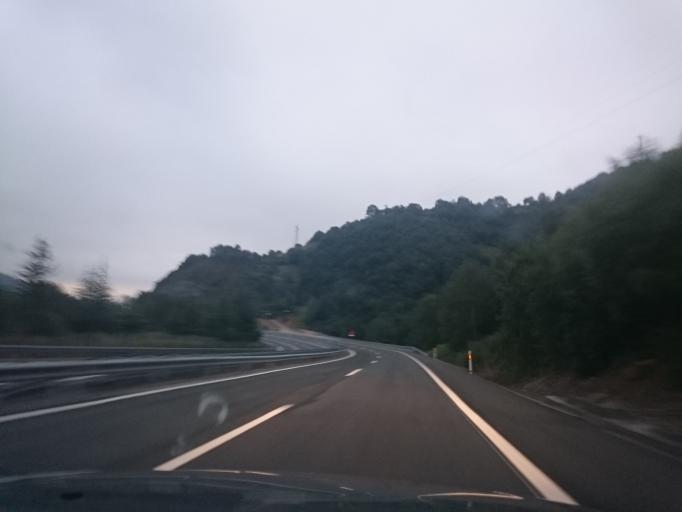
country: ES
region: Asturias
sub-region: Province of Asturias
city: Pola de Lena
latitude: 43.0866
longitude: -5.8236
